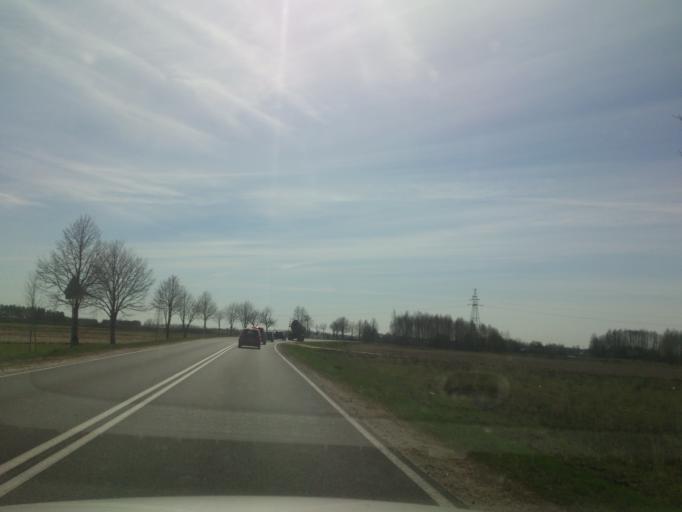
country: PL
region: Masovian Voivodeship
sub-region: Powiat mlawski
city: Szydlowo
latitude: 53.0922
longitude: 20.4189
